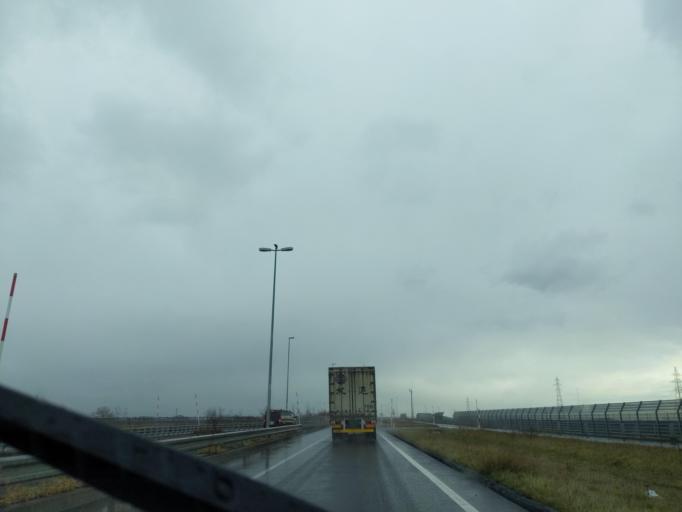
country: JP
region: Hokkaido
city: Ebetsu
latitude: 43.1267
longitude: 141.5742
